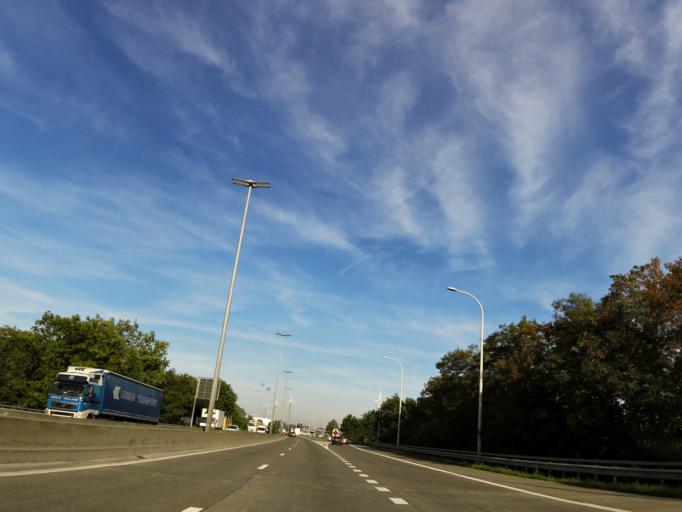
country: BE
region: Flanders
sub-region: Provincie Limburg
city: Tessenderlo
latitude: 51.0883
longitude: 5.1214
